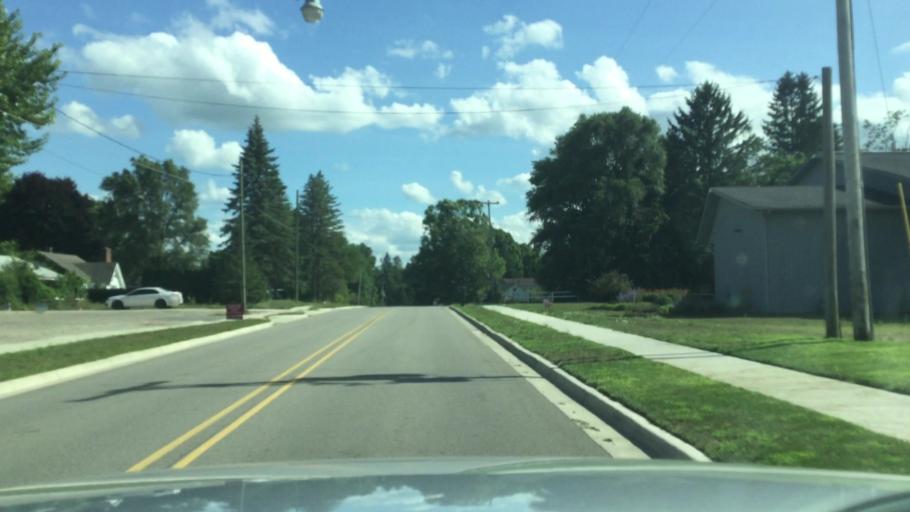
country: US
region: Michigan
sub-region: Ionia County
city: Belding
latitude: 43.0866
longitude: -85.2290
